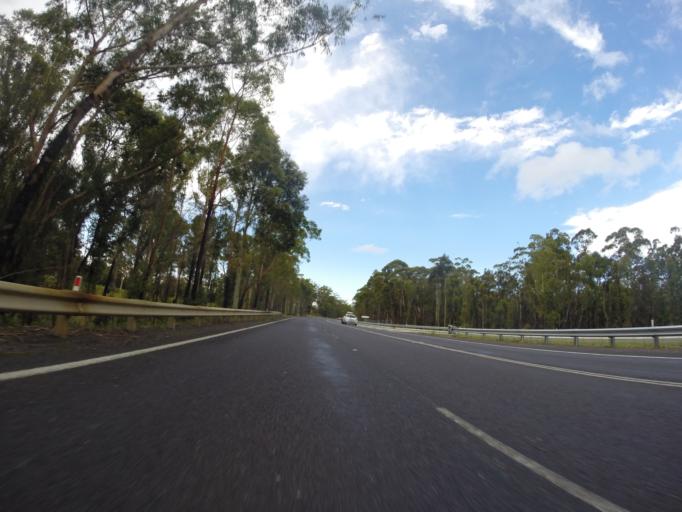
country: AU
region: New South Wales
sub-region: Shoalhaven Shire
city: Milton
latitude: -35.1234
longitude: 150.4771
